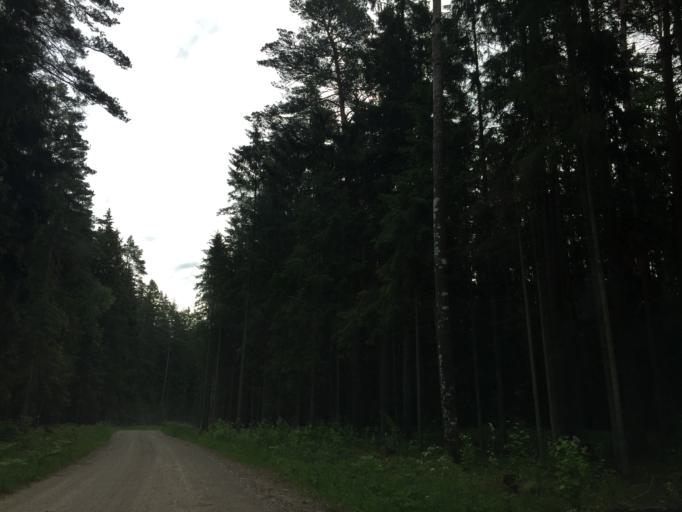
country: LV
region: Tukuma Rajons
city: Tukums
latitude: 57.0459
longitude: 23.1402
